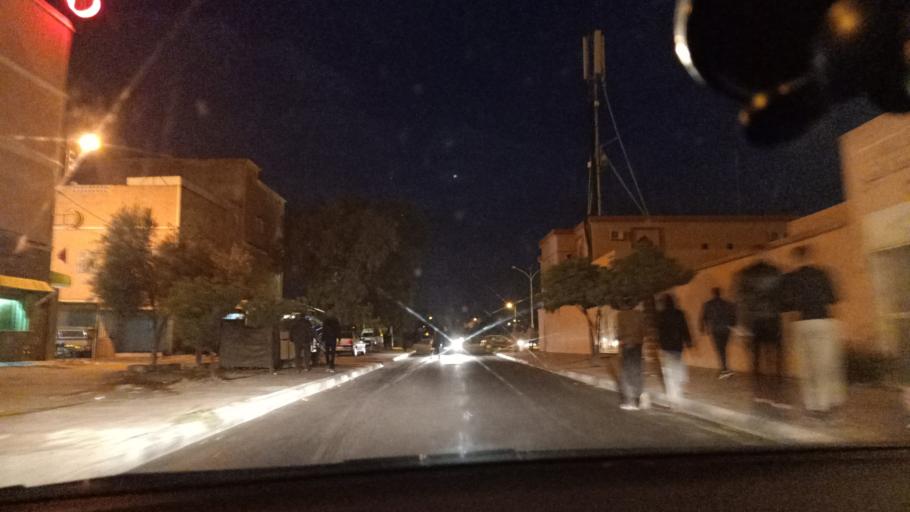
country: MA
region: Doukkala-Abda
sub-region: Safi
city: Youssoufia
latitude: 32.2516
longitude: -8.5342
